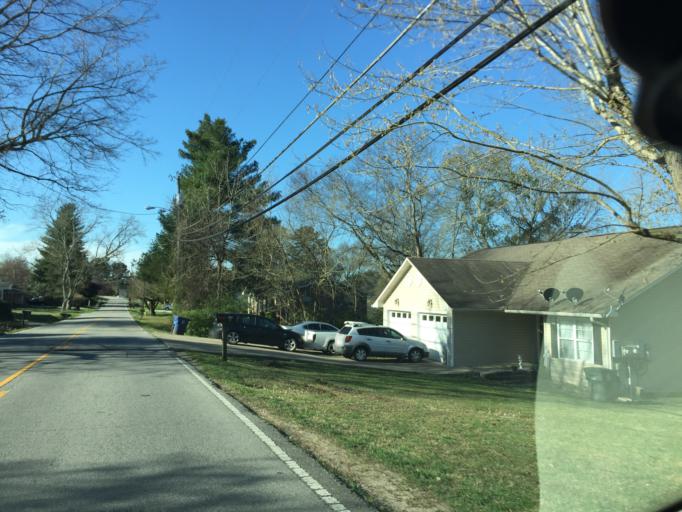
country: US
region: Tennessee
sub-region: Hamilton County
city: East Brainerd
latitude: 35.0242
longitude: -85.1715
